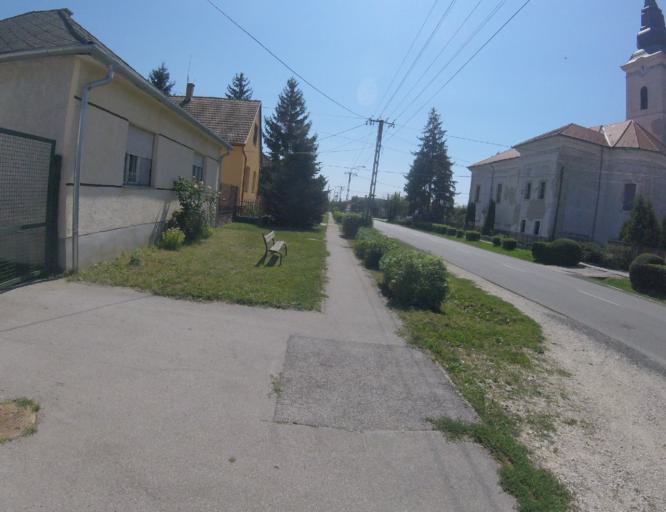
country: HU
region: Fejer
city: Pazmand
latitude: 47.2901
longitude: 18.6518
